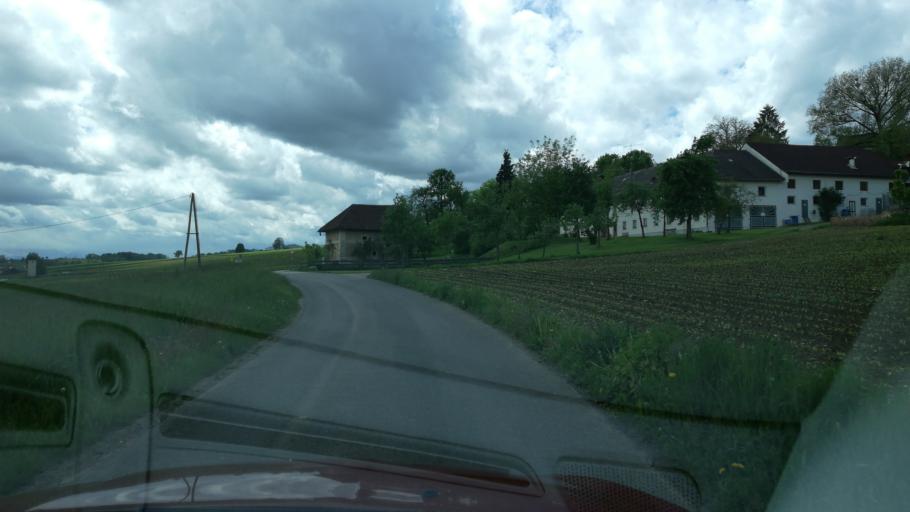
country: AT
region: Upper Austria
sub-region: Politischer Bezirk Linz-Land
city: Horsching
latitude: 48.1806
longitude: 14.2006
